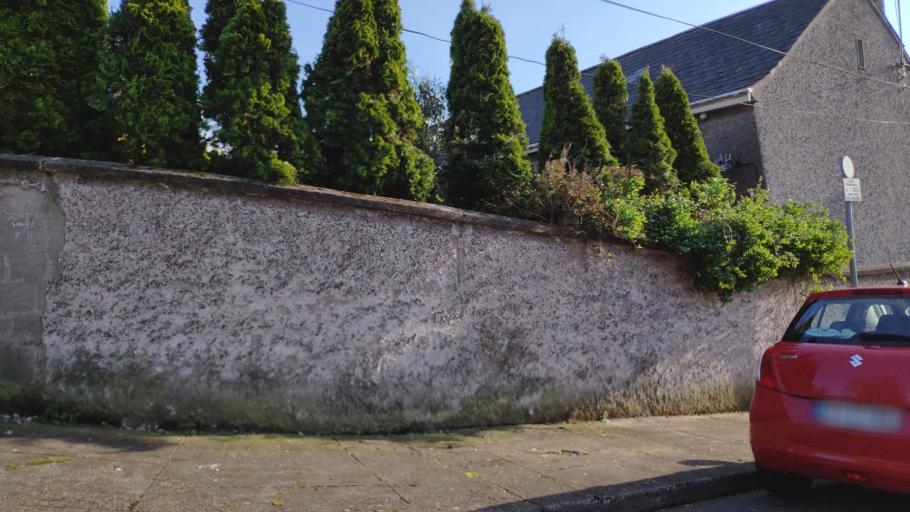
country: IE
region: Munster
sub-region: County Cork
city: Cork
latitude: 51.9075
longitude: -8.4701
